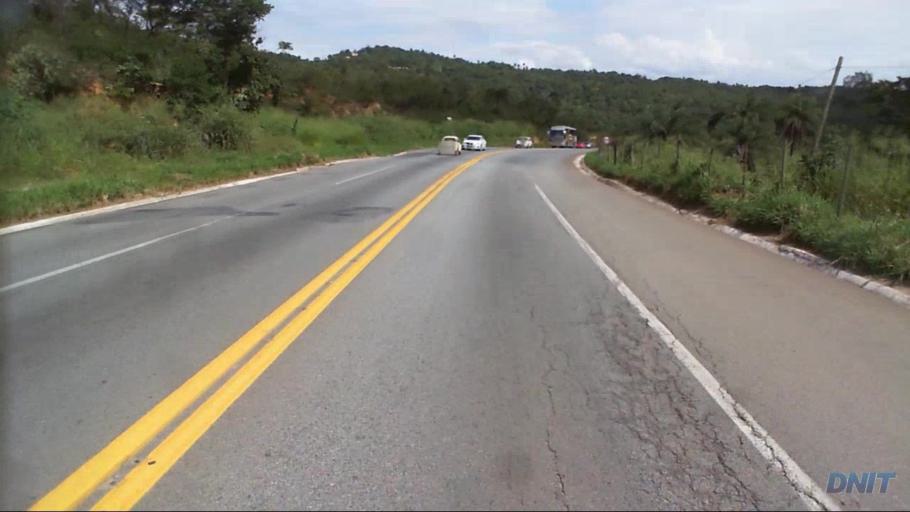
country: BR
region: Minas Gerais
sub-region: Santa Luzia
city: Santa Luzia
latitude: -19.8172
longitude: -43.8107
